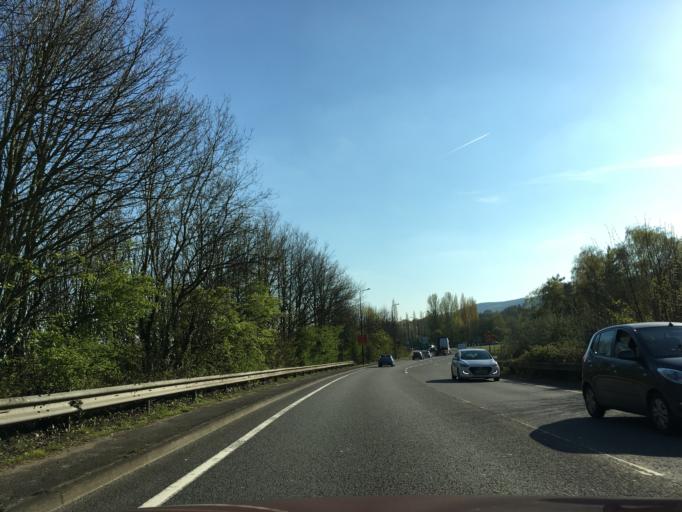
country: GB
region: Wales
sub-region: Torfaen County Borough
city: New Inn
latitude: 51.6736
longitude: -3.0173
